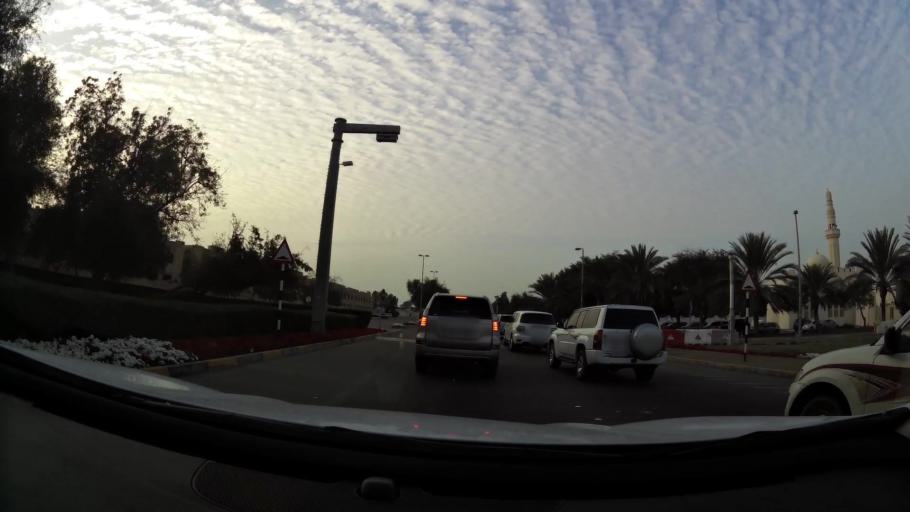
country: AE
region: Abu Dhabi
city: Abu Dhabi
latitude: 24.4326
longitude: 54.3840
